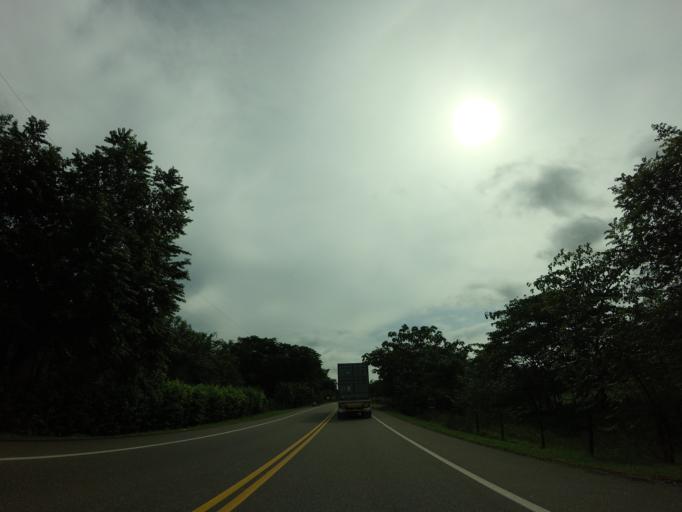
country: CO
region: Caldas
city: La Dorada
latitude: 5.4148
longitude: -74.6881
